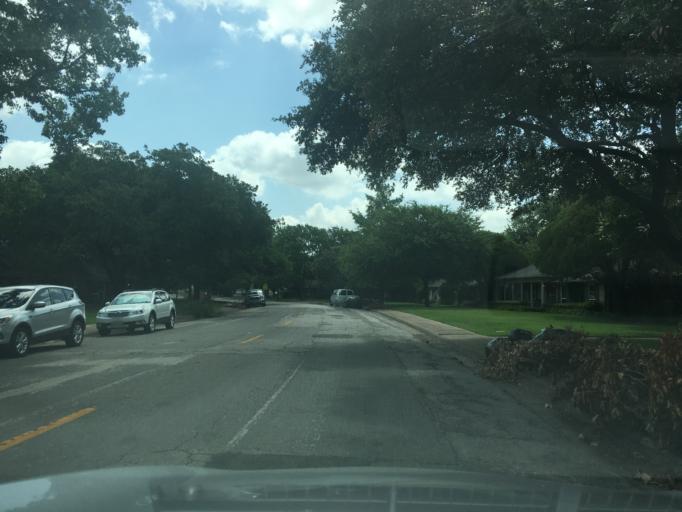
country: US
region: Texas
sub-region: Dallas County
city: Addison
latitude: 32.9214
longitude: -96.8229
